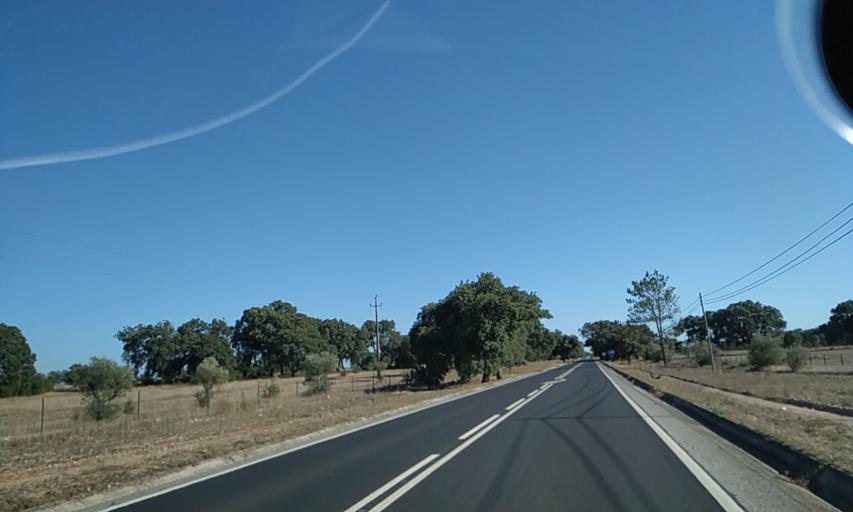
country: PT
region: Santarem
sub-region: Benavente
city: Poceirao
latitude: 38.8278
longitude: -8.8809
